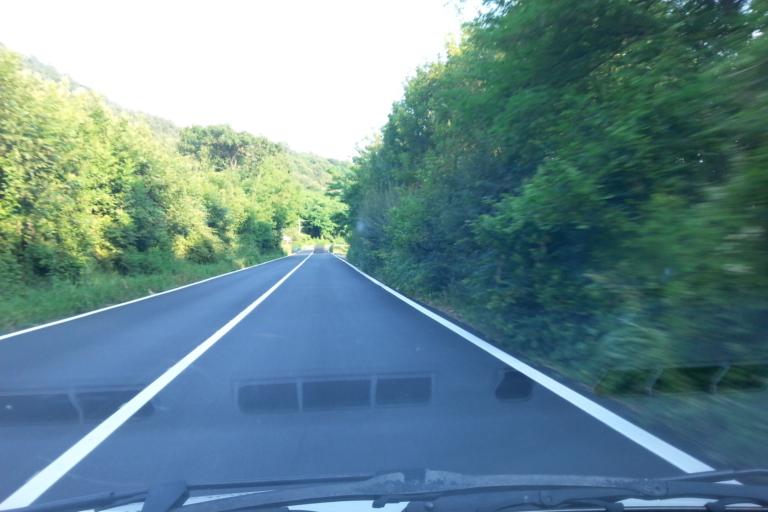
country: IT
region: Piedmont
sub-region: Provincia di Torino
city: Avigliana
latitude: 45.0585
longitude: 7.3942
